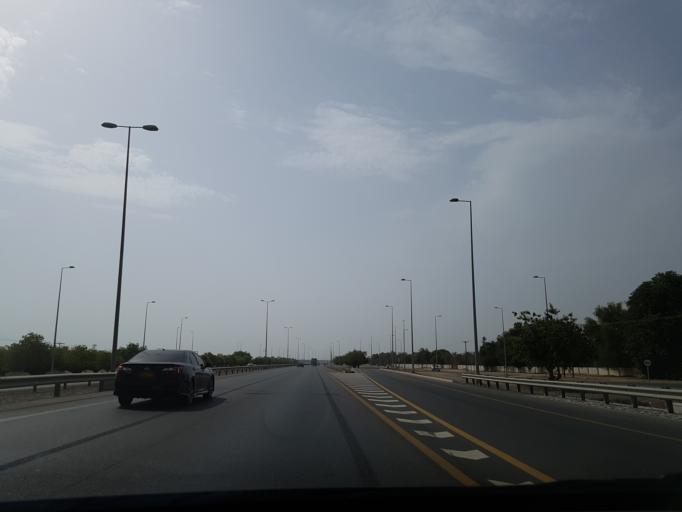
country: OM
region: Al Batinah
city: Saham
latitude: 24.1158
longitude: 56.9085
